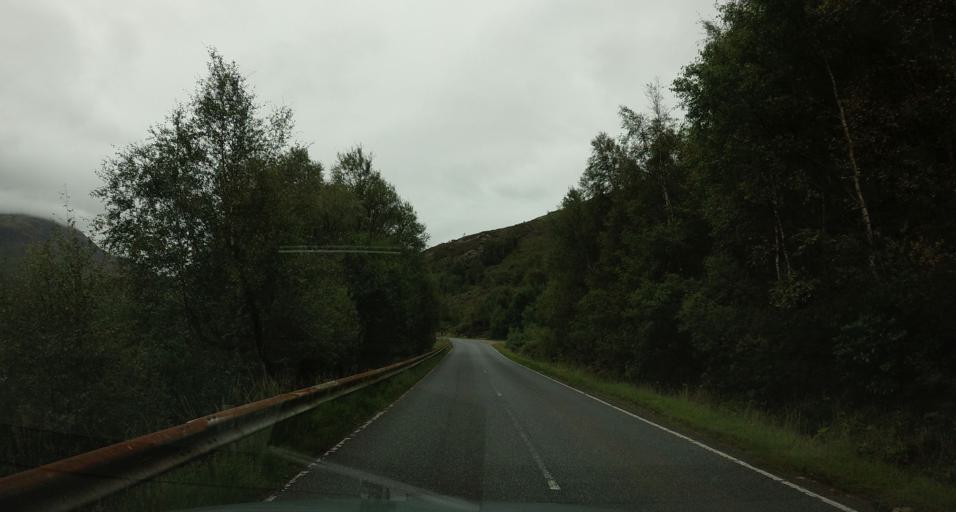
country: GB
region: Scotland
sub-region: Highland
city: Fort William
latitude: 56.7106
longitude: -4.9855
